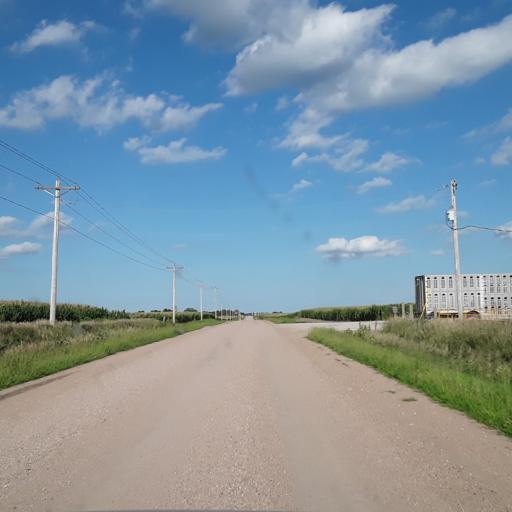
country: US
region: Nebraska
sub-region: Hall County
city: Wood River
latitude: 40.9168
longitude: -98.5995
